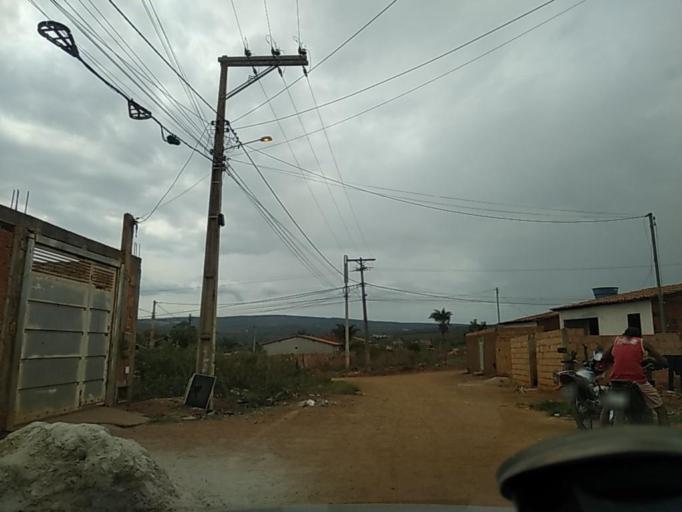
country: BR
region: Bahia
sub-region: Caetite
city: Caetite
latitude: -14.0490
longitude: -42.4755
